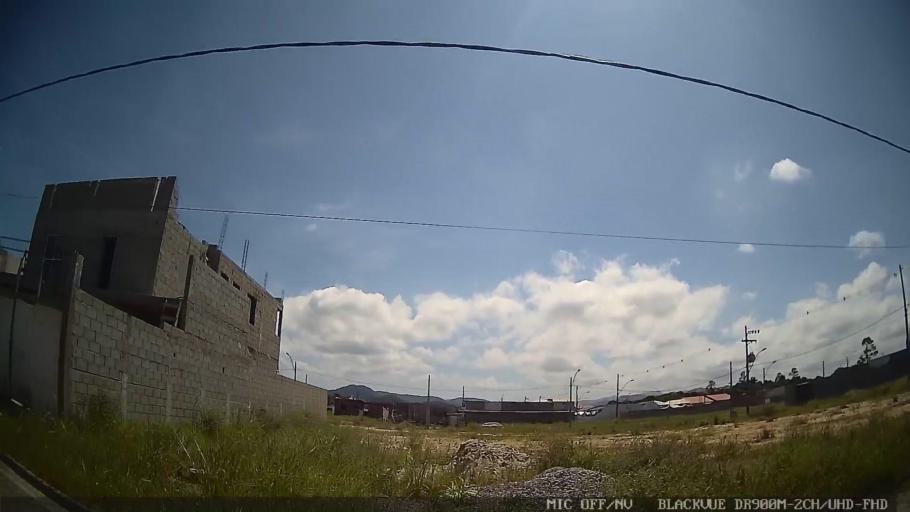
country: BR
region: Sao Paulo
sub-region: Peruibe
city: Peruibe
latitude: -24.3016
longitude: -46.9973
